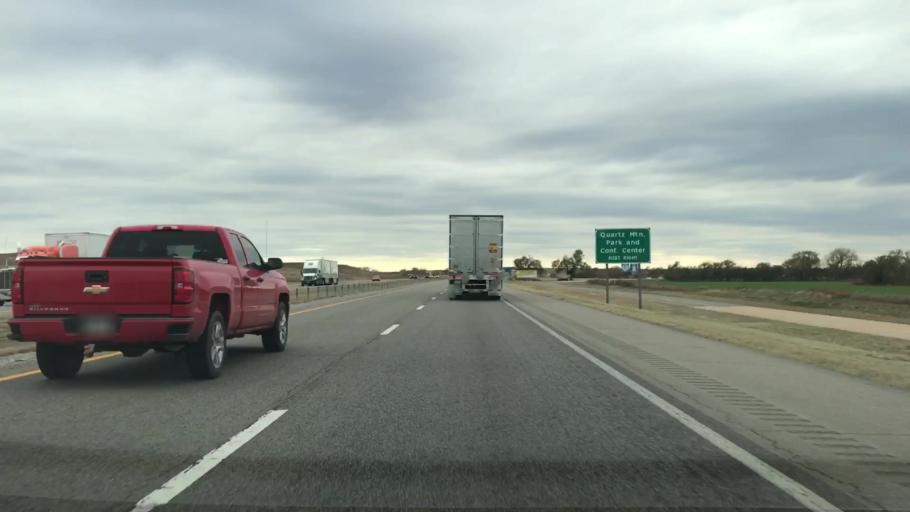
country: US
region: Oklahoma
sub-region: Washita County
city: Burns Flat
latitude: 35.4536
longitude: -99.1564
